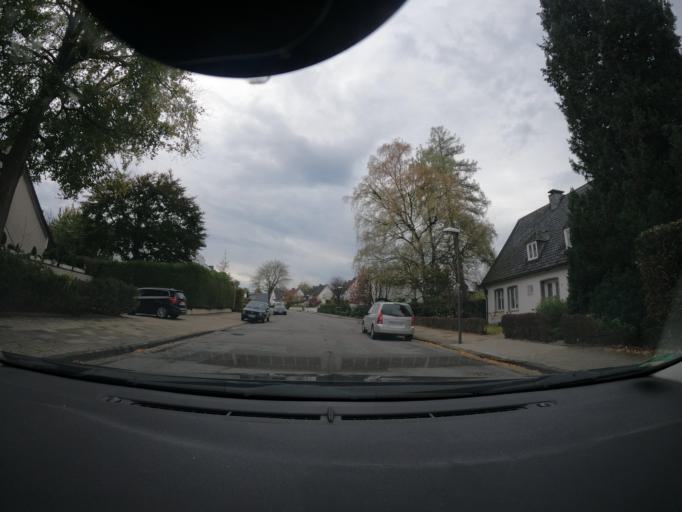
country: DE
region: North Rhine-Westphalia
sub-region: Regierungsbezirk Koln
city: Aachen
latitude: 50.7506
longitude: 6.0921
